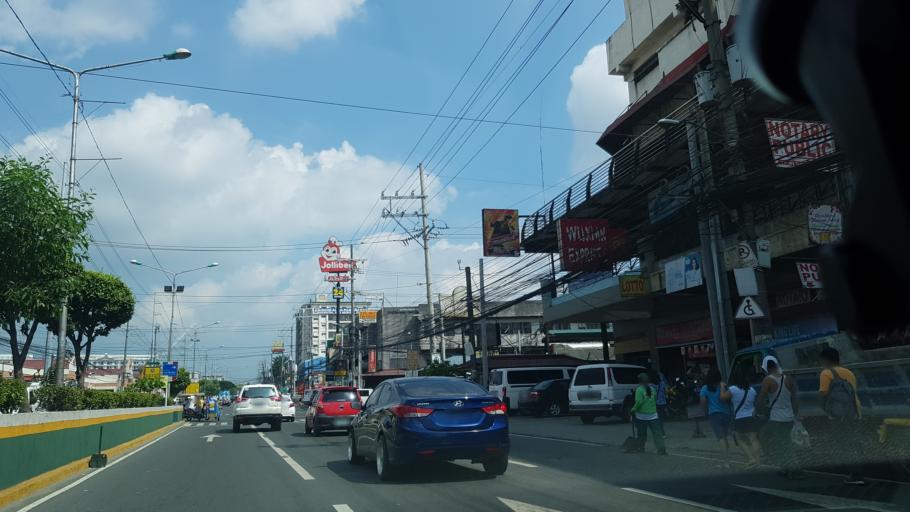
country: PH
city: Sambayanihan People's Village
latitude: 14.4659
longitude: 121.0173
